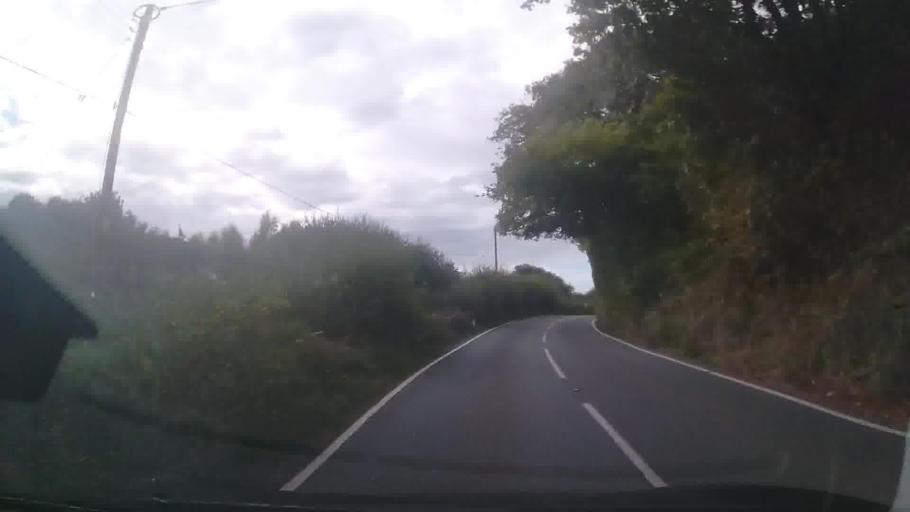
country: GB
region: Wales
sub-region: Gwynedd
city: Dolgellau
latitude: 52.7539
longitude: -3.9342
